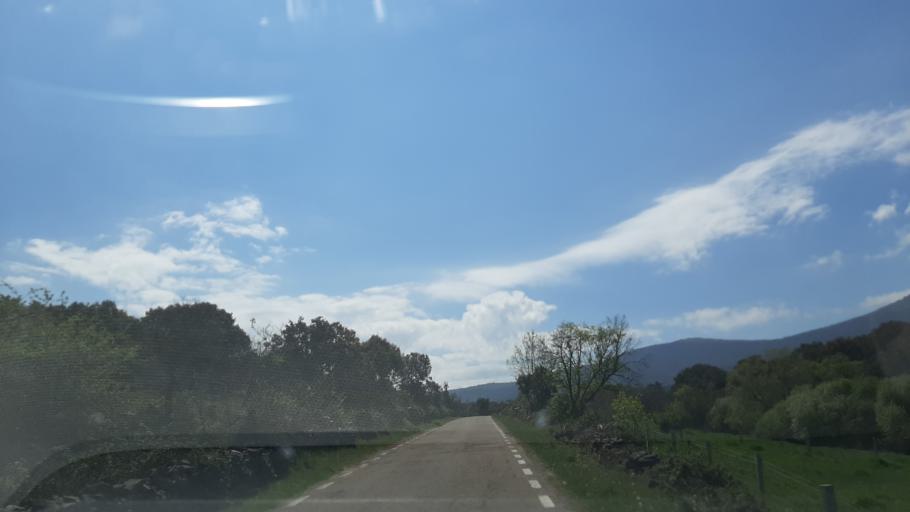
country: ES
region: Castille and Leon
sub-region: Provincia de Salamanca
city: Tejeda y Segoyuela
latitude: 40.6212
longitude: -6.0207
